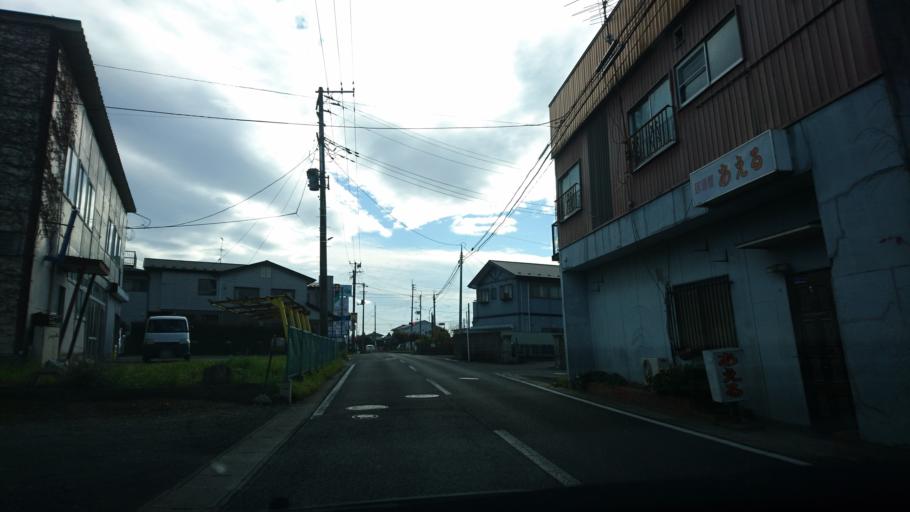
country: JP
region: Miyagi
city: Wakuya
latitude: 38.6822
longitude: 141.1956
